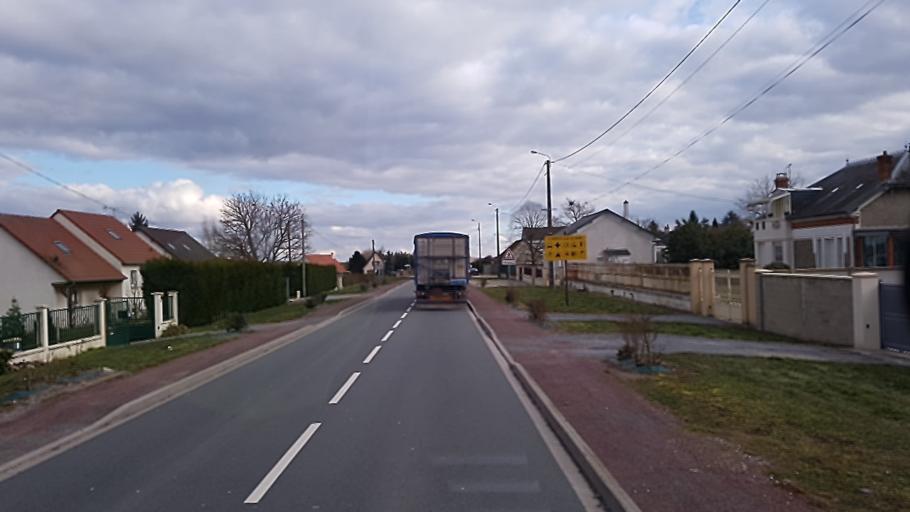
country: FR
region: Picardie
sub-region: Departement de l'Aisne
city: Saint-Erme-Outre-et-Ramecourt
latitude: 49.4672
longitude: 3.8182
